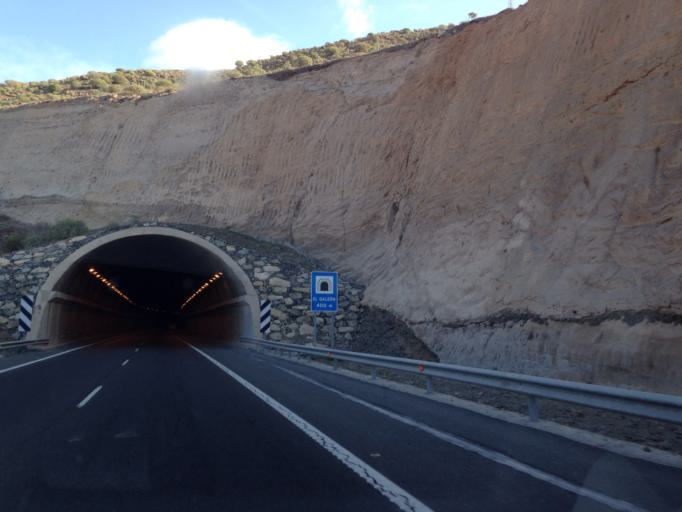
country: ES
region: Canary Islands
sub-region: Provincia de Las Palmas
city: Puerto Rico
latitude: 27.7678
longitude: -15.6623
